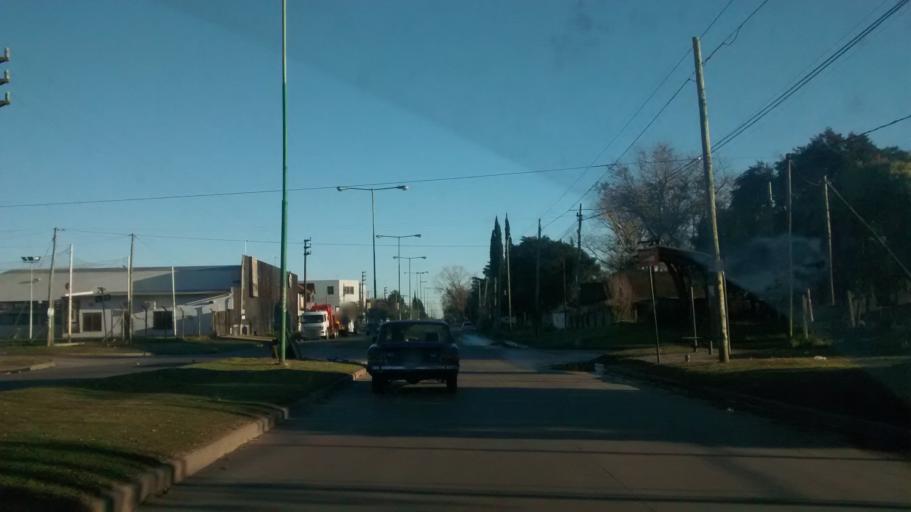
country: AR
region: Buenos Aires
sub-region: Partido de La Plata
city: La Plata
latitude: -34.9469
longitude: -57.9898
